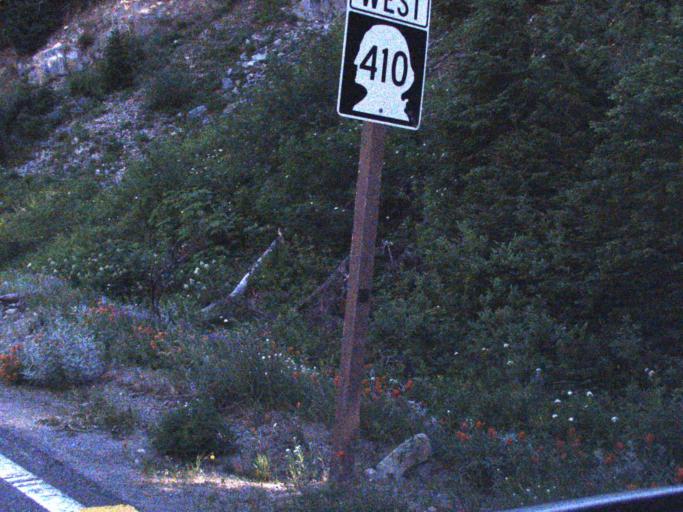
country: US
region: Washington
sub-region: King County
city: Enumclaw
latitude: 46.8689
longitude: -121.5403
